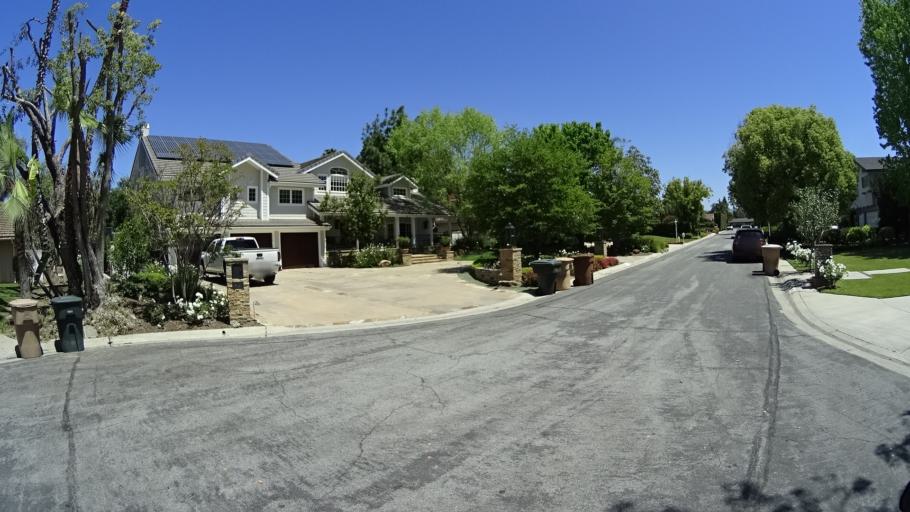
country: US
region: California
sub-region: Orange County
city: Villa Park
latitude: 33.8130
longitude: -117.8125
